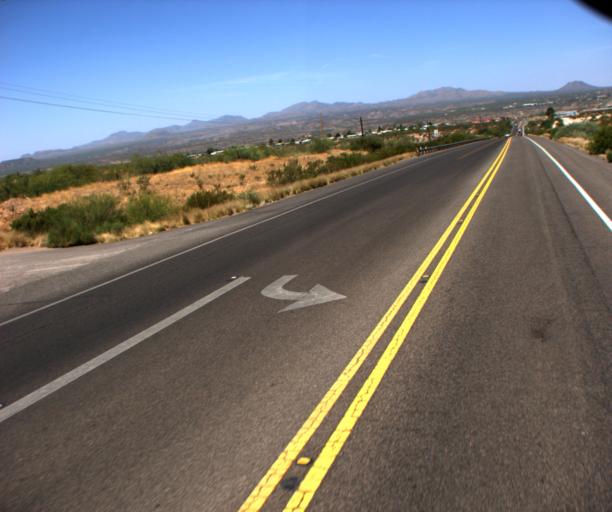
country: US
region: Arizona
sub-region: Gila County
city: Peridot
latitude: 33.2920
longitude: -110.4284
